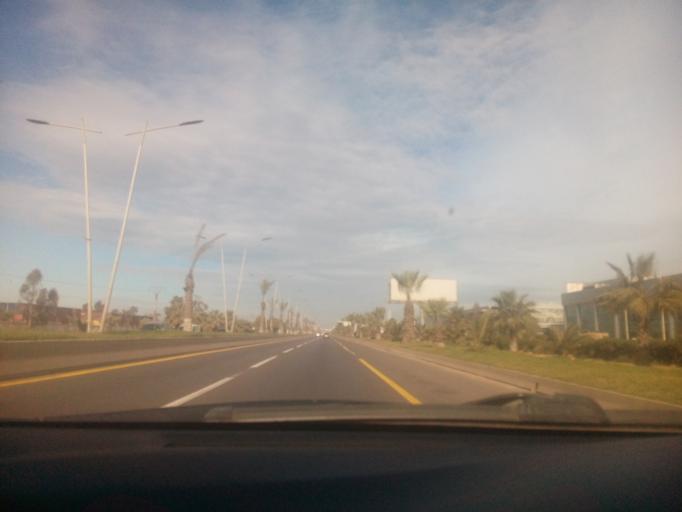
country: DZ
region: Oran
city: Es Senia
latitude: 35.6451
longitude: -0.5898
